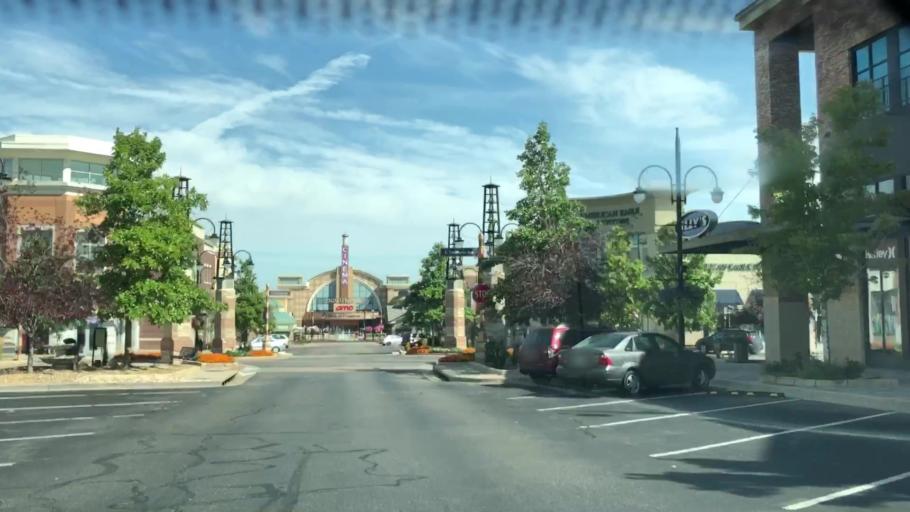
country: US
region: Colorado
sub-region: Douglas County
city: Parker
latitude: 39.6040
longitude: -104.7089
